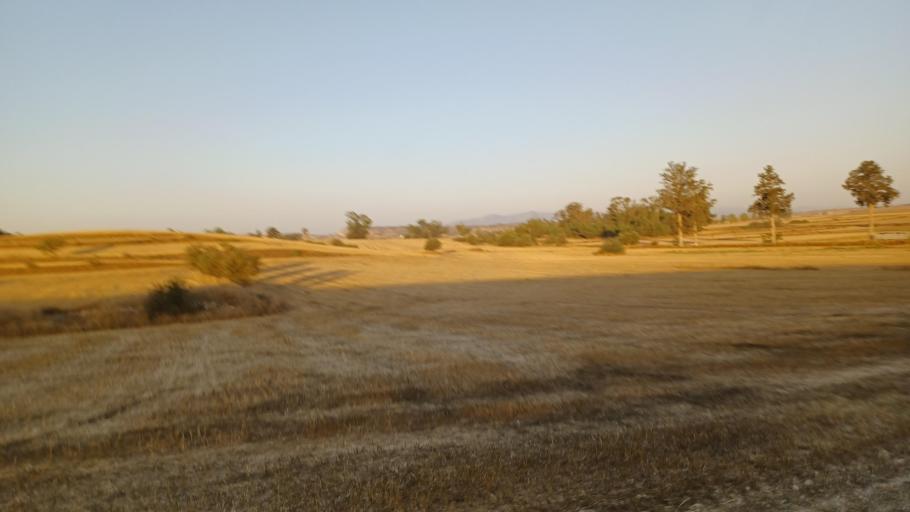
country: CY
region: Lefkosia
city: Lympia
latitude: 35.0368
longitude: 33.4964
